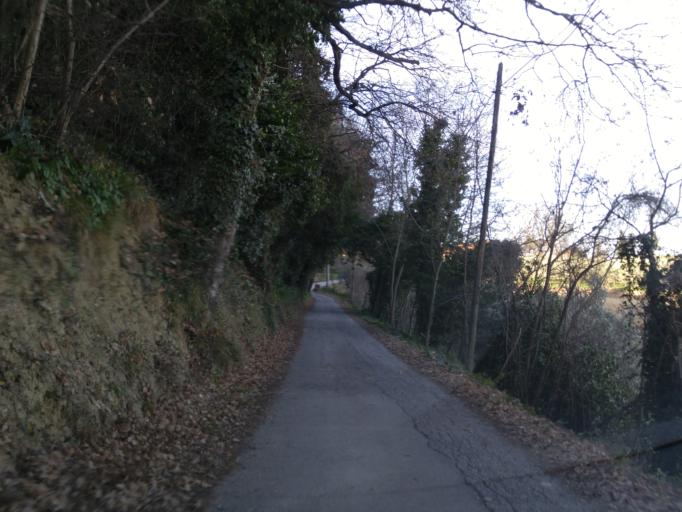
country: IT
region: The Marches
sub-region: Provincia di Pesaro e Urbino
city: Cartoceto
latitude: 43.7625
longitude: 12.8834
